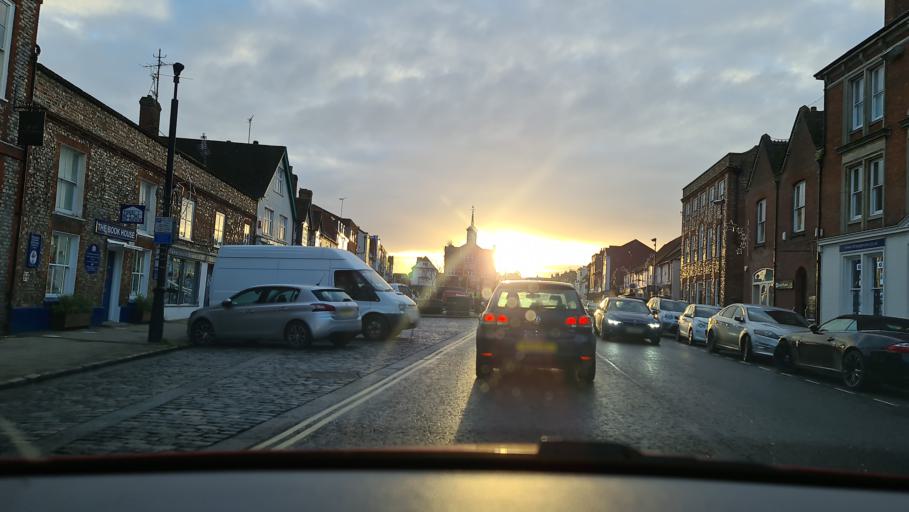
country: GB
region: England
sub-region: Oxfordshire
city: Thame
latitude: 51.7486
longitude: -0.9800
